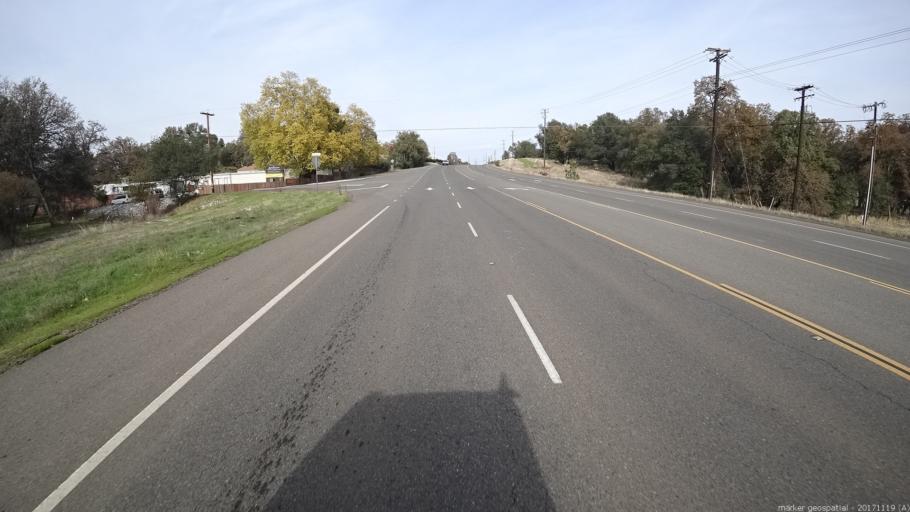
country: US
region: California
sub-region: Shasta County
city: Anderson
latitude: 40.4762
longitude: -122.2929
